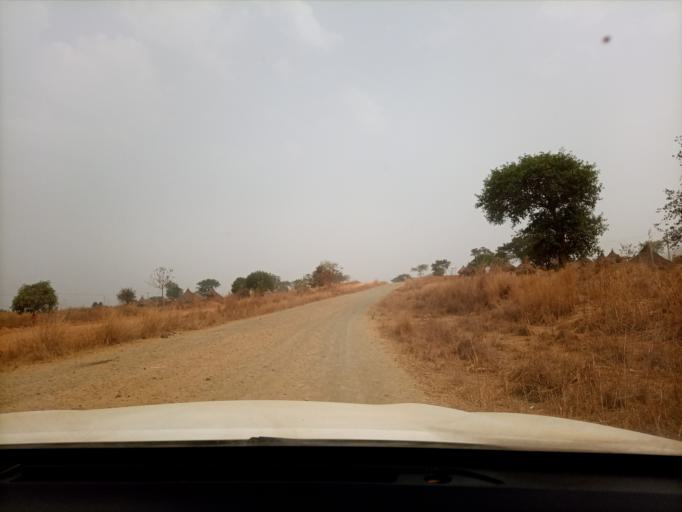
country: ET
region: Oromiya
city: Mendi
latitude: 10.1825
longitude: 35.0905
